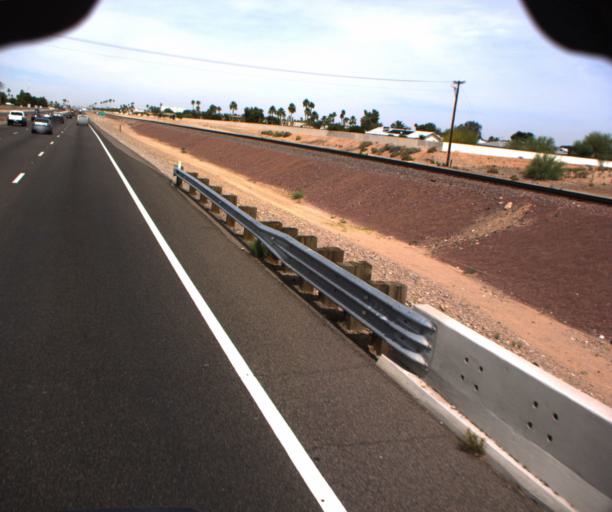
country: US
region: Arizona
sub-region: Maricopa County
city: Sun City
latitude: 33.5950
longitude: -112.2631
